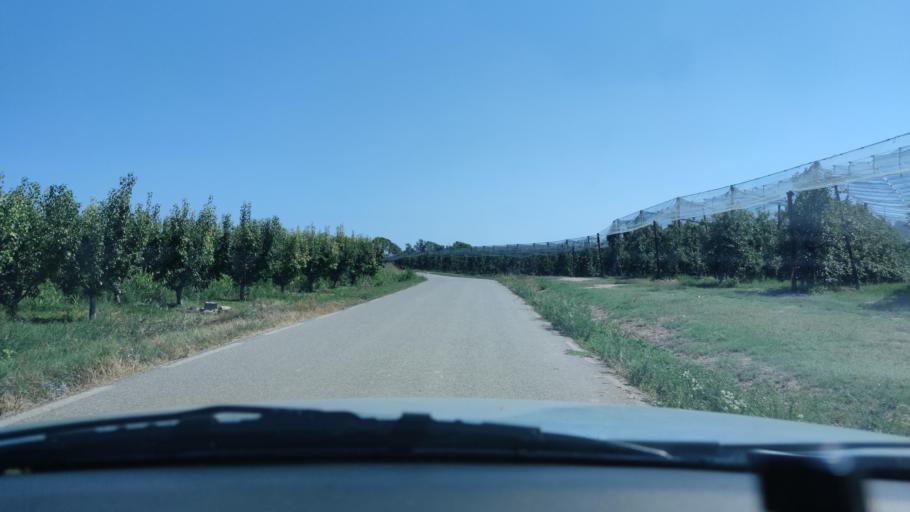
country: ES
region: Catalonia
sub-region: Provincia de Lleida
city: Torrefarrera
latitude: 41.6839
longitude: 0.6260
